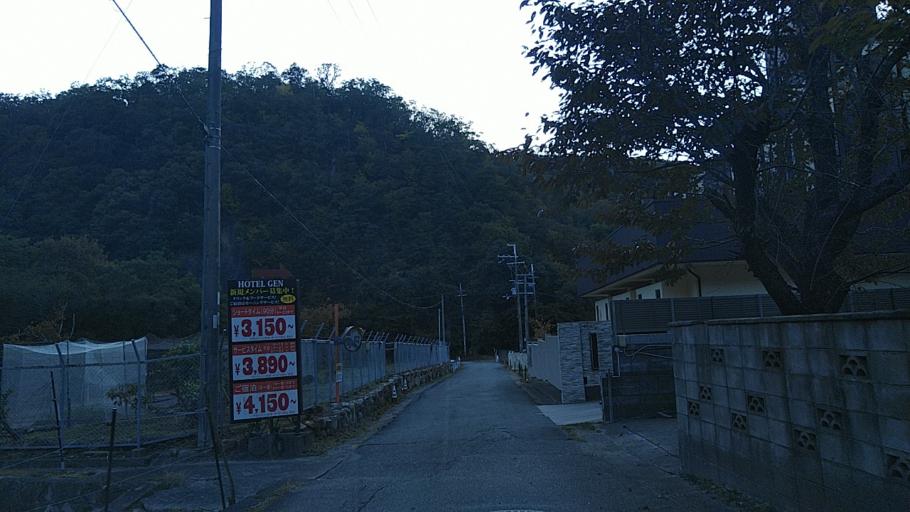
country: JP
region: Osaka
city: Ikeda
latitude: 34.9422
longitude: 135.4099
